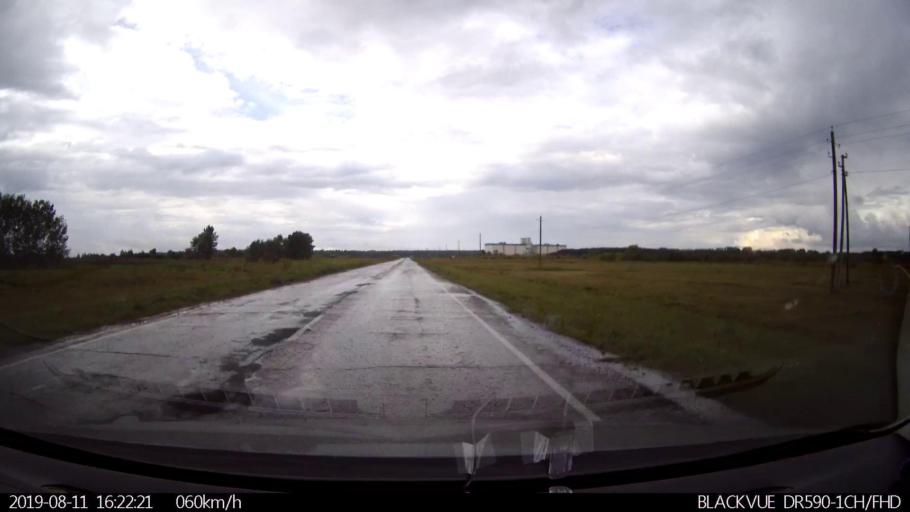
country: RU
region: Ulyanovsk
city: Mayna
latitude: 54.0873
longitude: 47.5933
